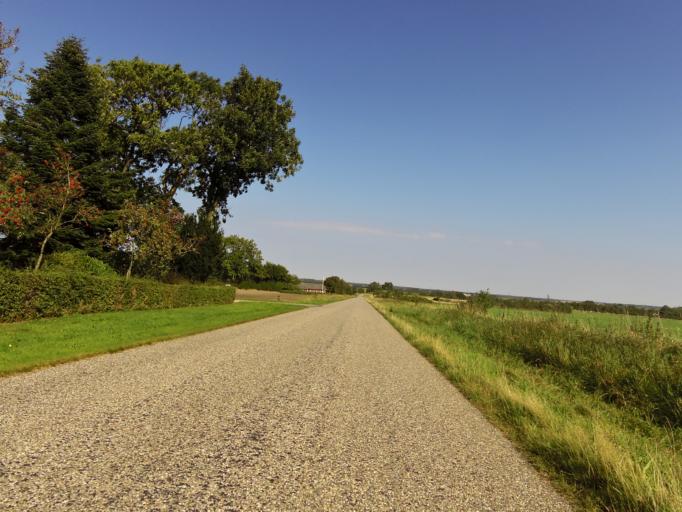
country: DK
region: South Denmark
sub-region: Vejen Kommune
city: Rodding
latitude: 55.3281
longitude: 9.1174
